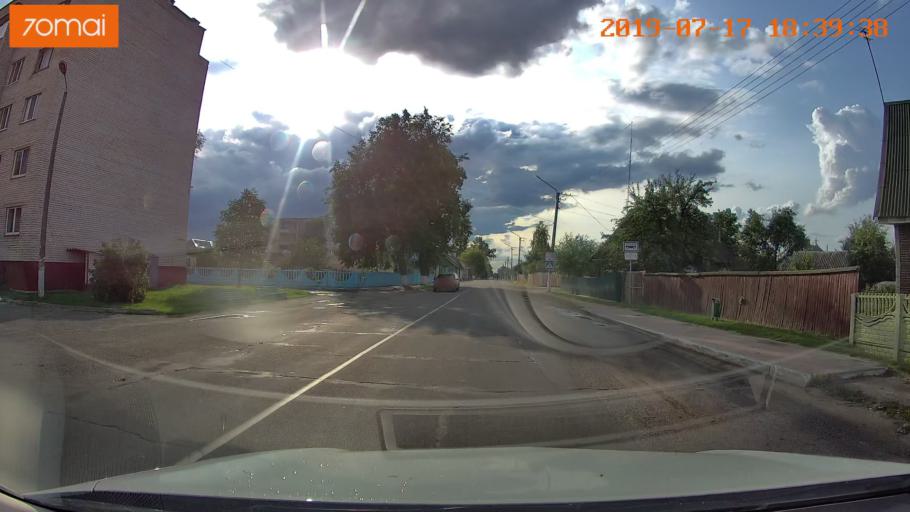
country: BY
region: Mogilev
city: Asipovichy
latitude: 53.2984
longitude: 28.6552
